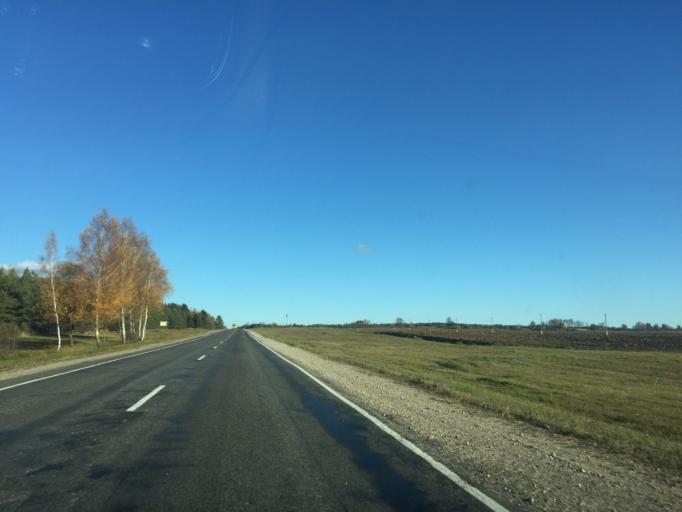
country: BY
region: Vitebsk
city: Dzisna
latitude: 55.2387
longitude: 28.0443
